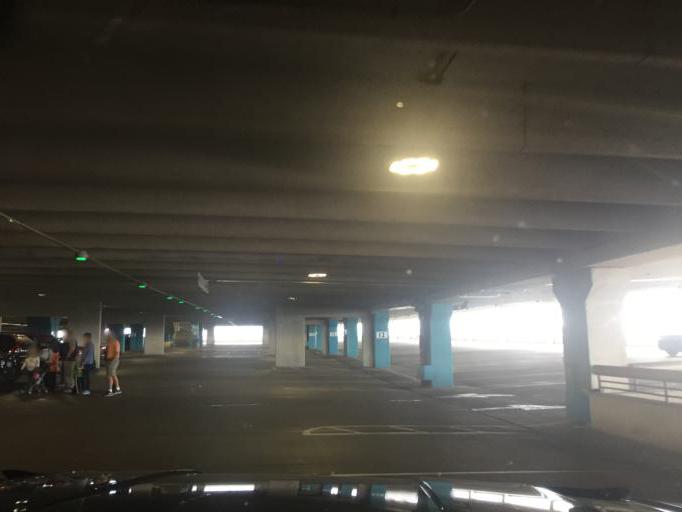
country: US
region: Minnesota
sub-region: Hennepin County
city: Richfield
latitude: 44.8548
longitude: -93.2385
